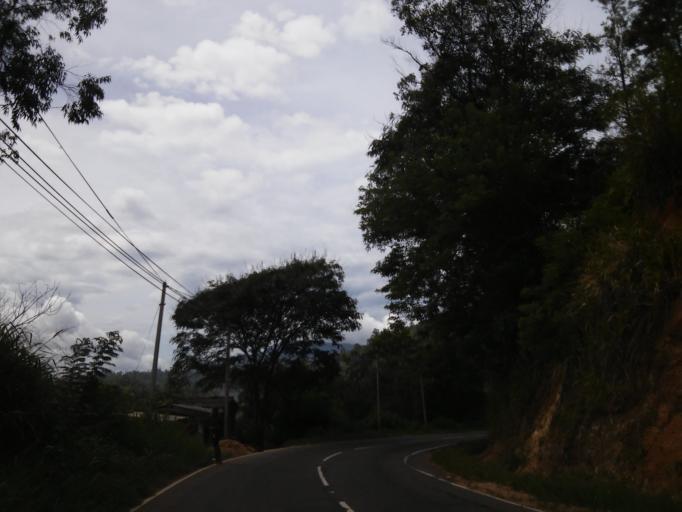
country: LK
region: Uva
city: Haputale
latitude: 6.8716
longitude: 80.9514
